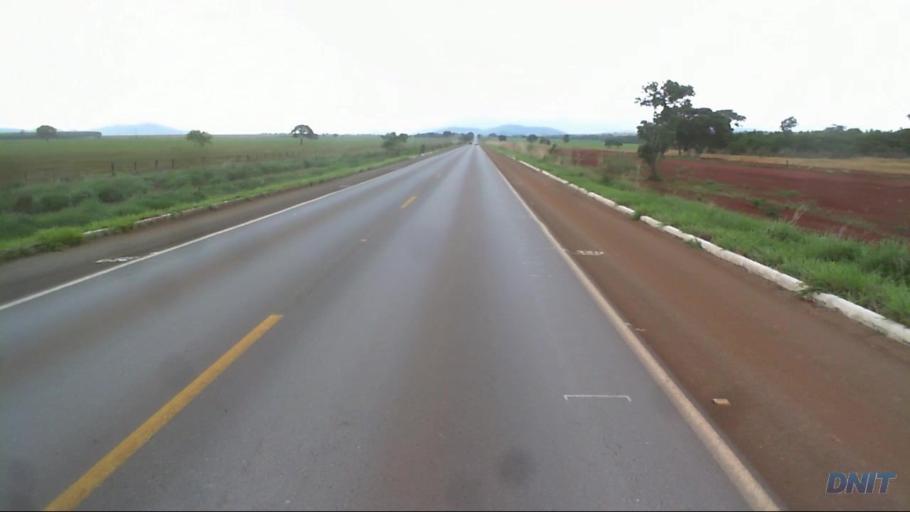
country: BR
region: Goias
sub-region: Barro Alto
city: Barro Alto
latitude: -14.8194
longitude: -49.0400
